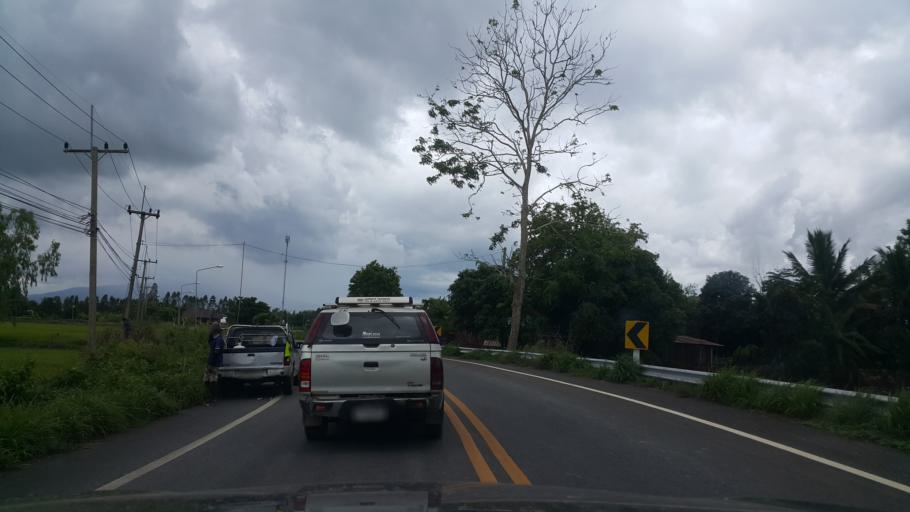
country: TH
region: Sukhothai
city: Sukhothai
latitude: 16.9193
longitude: 99.8539
